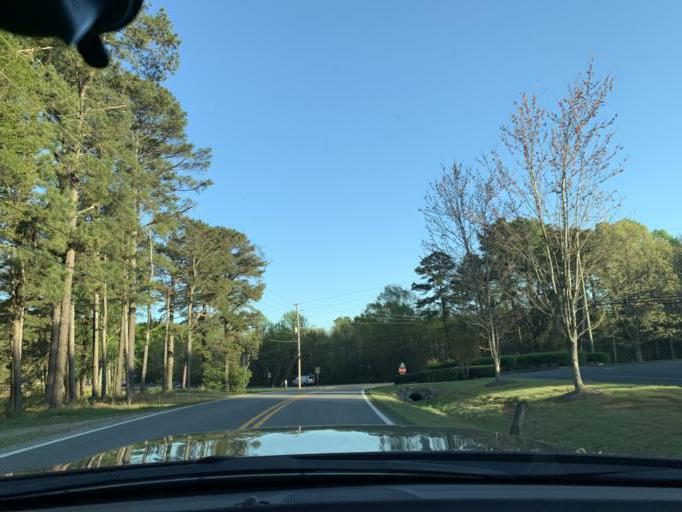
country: US
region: Georgia
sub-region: Forsyth County
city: Cumming
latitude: 34.2410
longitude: -84.1788
